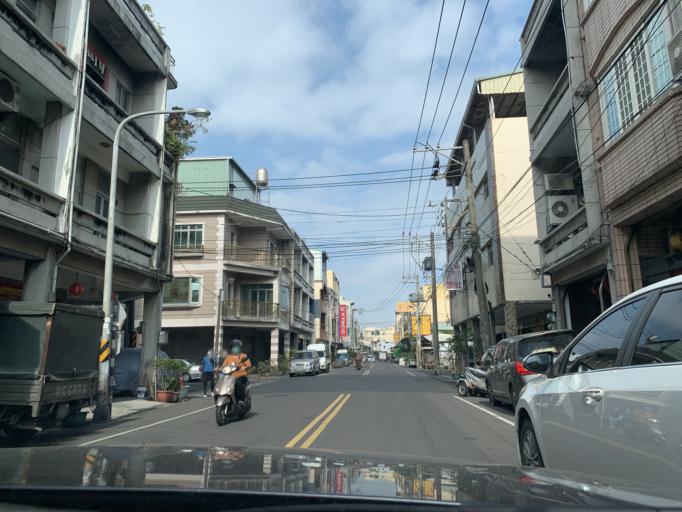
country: TW
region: Taiwan
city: Fengshan
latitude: 22.4666
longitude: 120.4469
